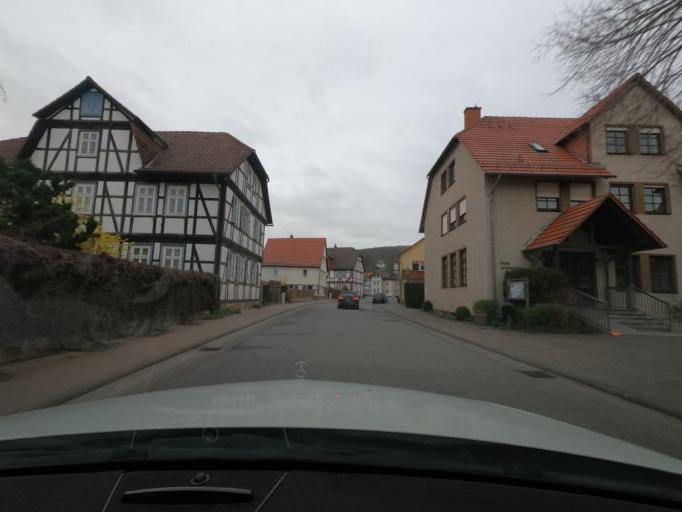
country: DE
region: Hesse
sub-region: Regierungsbezirk Kassel
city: Eschwege
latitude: 51.2036
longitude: 10.0641
